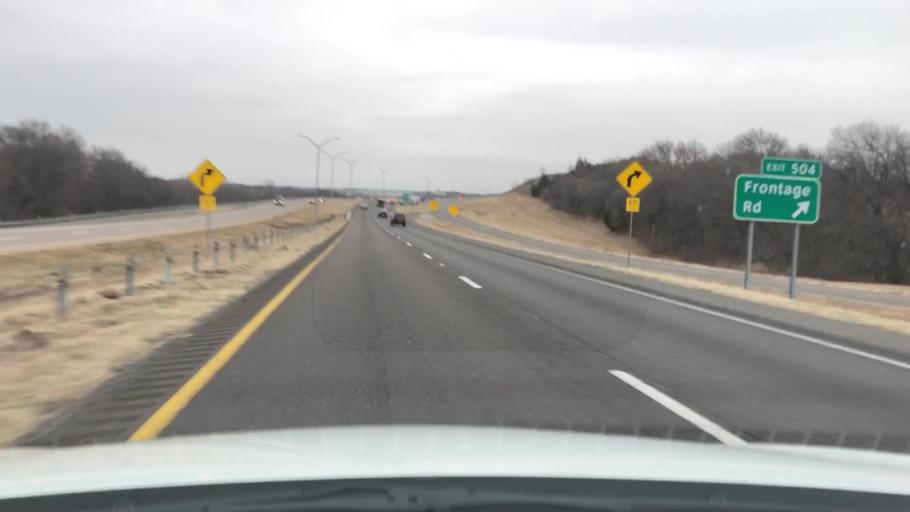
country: US
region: Texas
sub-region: Cooke County
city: Gainesville
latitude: 33.7212
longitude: -97.1612
